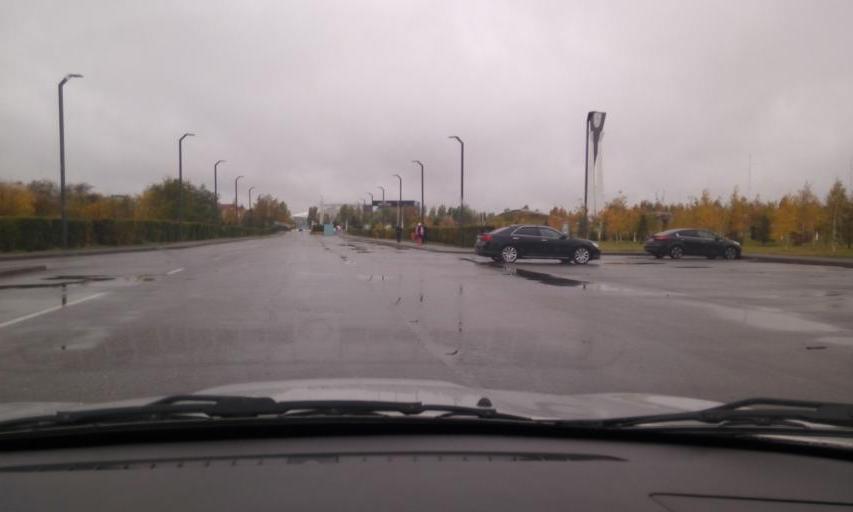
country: KZ
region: Astana Qalasy
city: Astana
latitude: 51.1531
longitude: 71.4173
